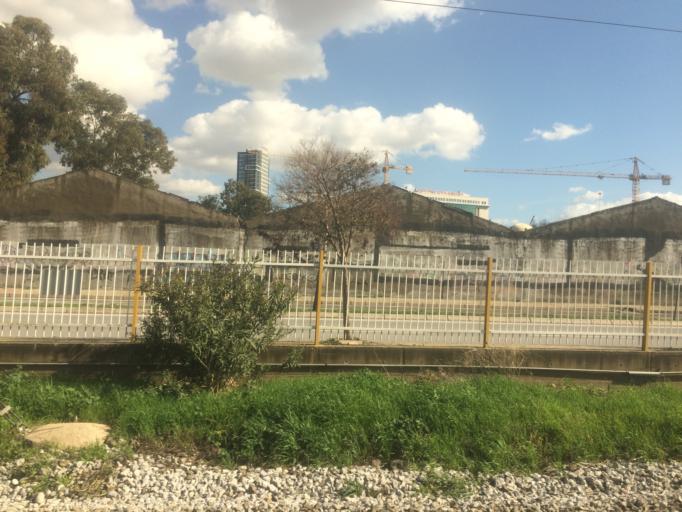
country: TR
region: Izmir
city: Buca
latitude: 38.4439
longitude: 27.1736
